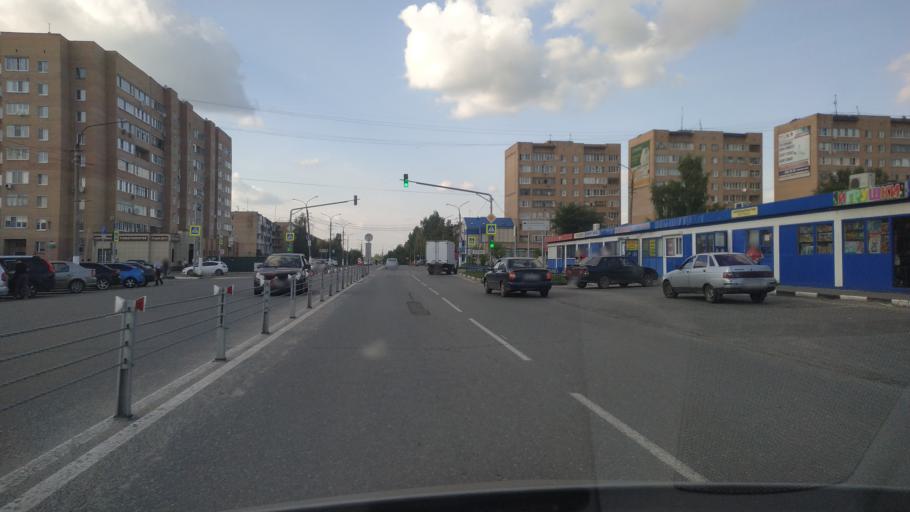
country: RU
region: Moskovskaya
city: Shatura
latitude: 55.5766
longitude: 39.5210
